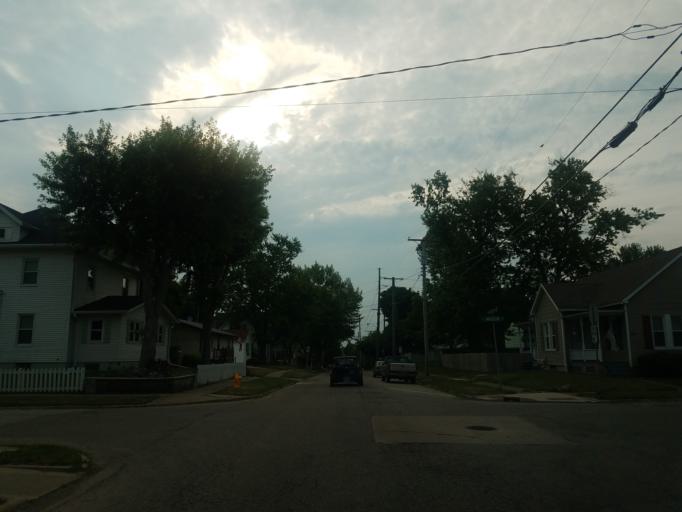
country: US
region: Illinois
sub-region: McLean County
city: Bloomington
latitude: 40.4729
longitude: -88.9991
